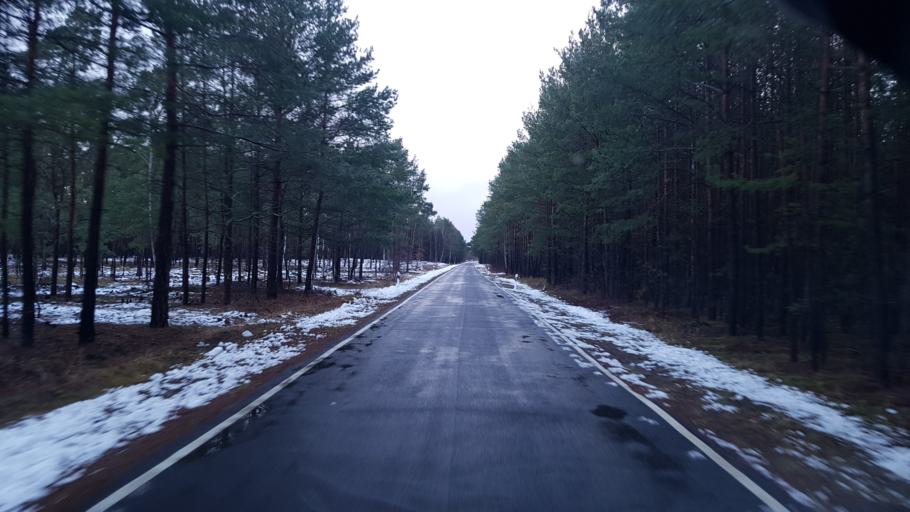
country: DE
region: Brandenburg
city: Janschwalde
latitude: 51.8434
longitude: 14.5082
